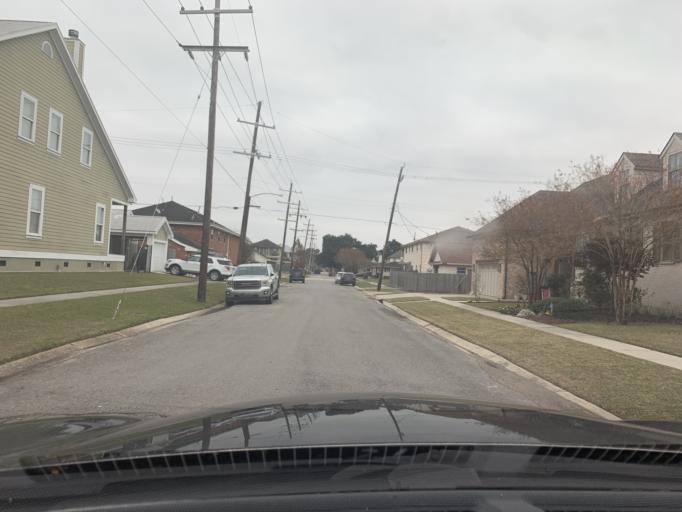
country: US
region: Louisiana
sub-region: Jefferson Parish
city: Metairie
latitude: 30.0157
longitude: -90.1045
